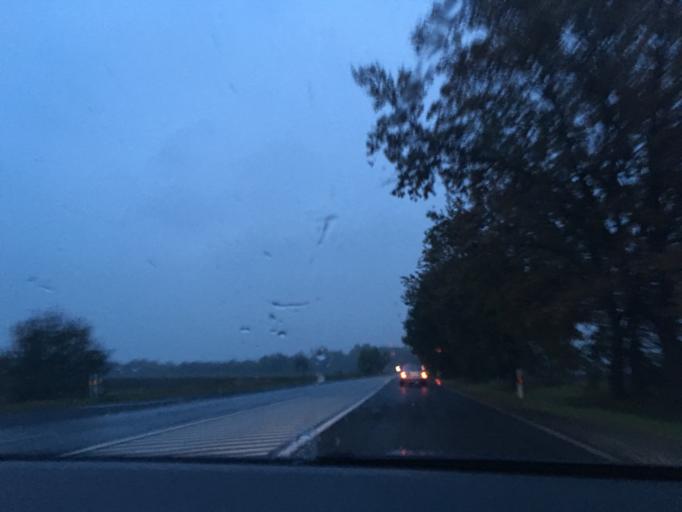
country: HU
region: Pest
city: Monor
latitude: 47.3189
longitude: 19.4761
